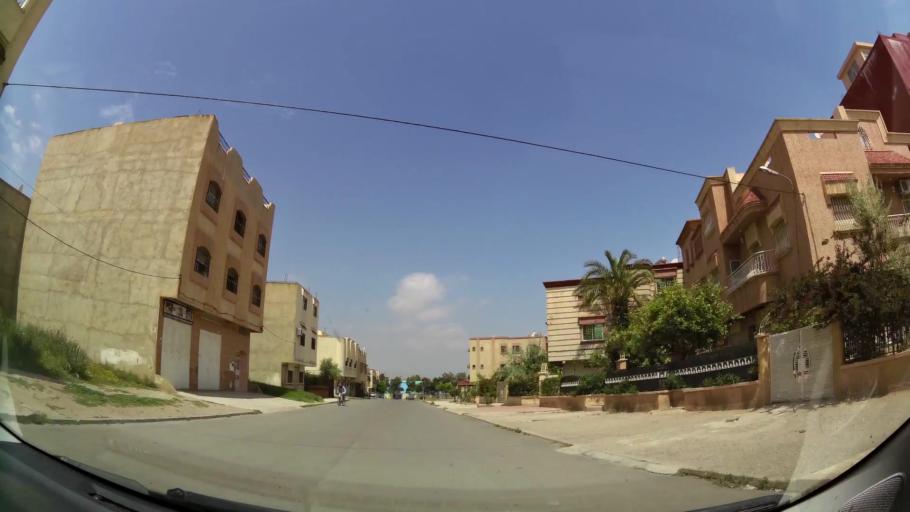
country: MA
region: Oriental
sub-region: Oujda-Angad
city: Oujda
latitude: 34.6850
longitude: -1.8819
